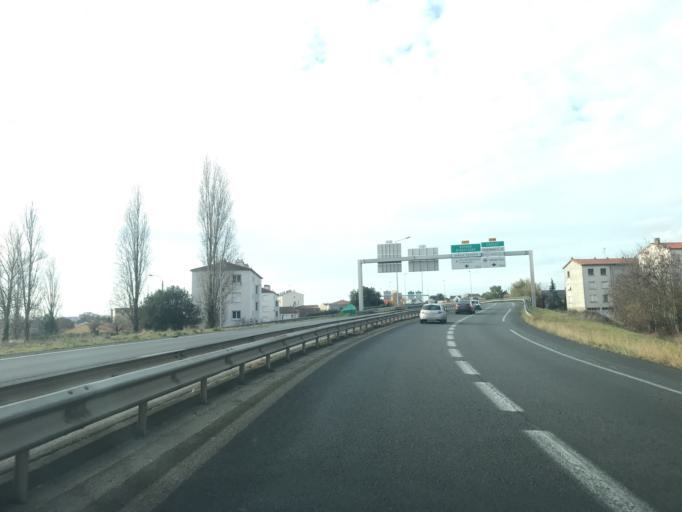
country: FR
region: Poitou-Charentes
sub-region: Departement des Deux-Sevres
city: Niort
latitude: 46.3333
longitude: -0.4688
